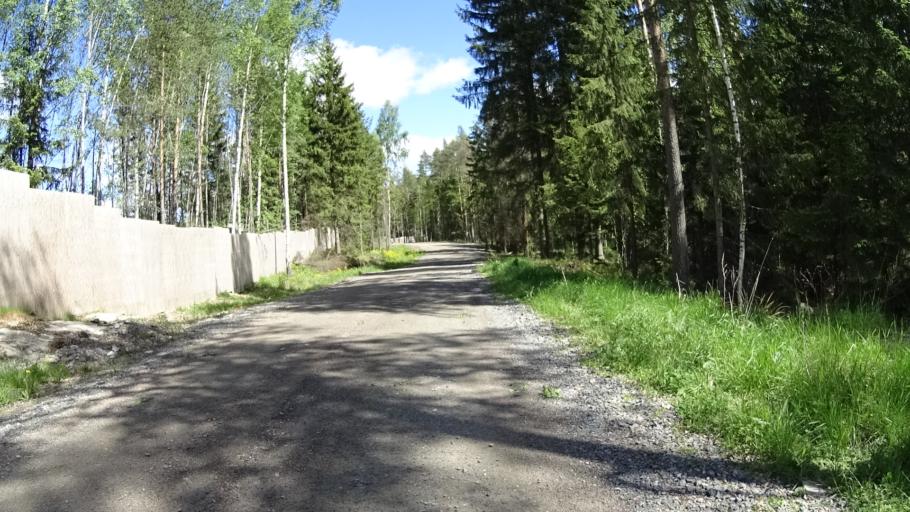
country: FI
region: Uusimaa
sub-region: Helsinki
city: Espoo
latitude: 60.2060
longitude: 24.6150
